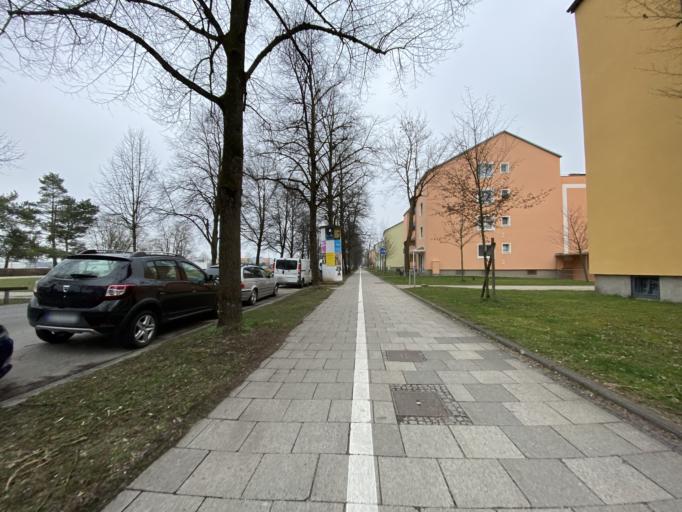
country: DE
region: Bavaria
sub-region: Upper Bavaria
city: Oberschleissheim
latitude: 48.2184
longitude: 11.5613
